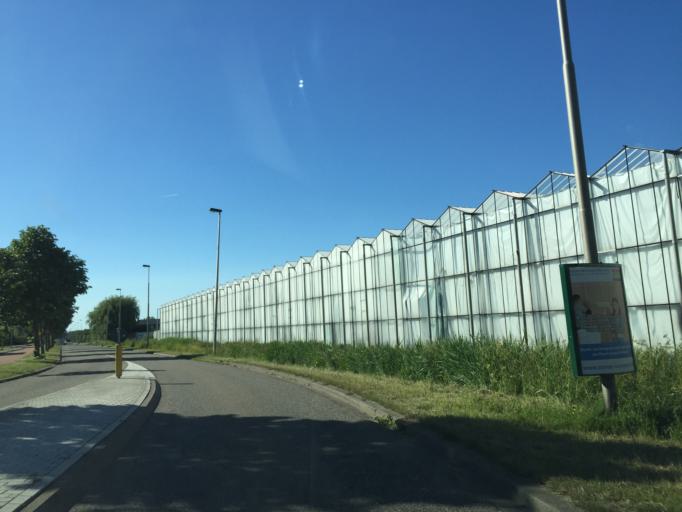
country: NL
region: South Holland
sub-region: Gemeente Lansingerland
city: Bergschenhoek
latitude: 51.9938
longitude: 4.5129
